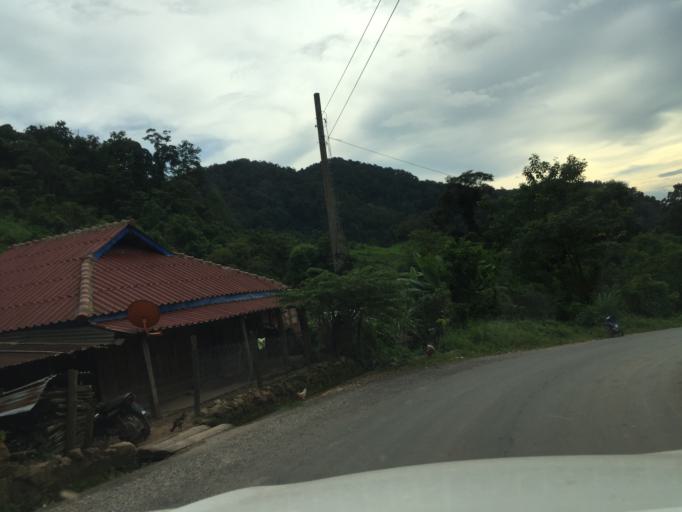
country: LA
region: Phongsali
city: Phongsali
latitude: 21.3452
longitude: 102.0517
